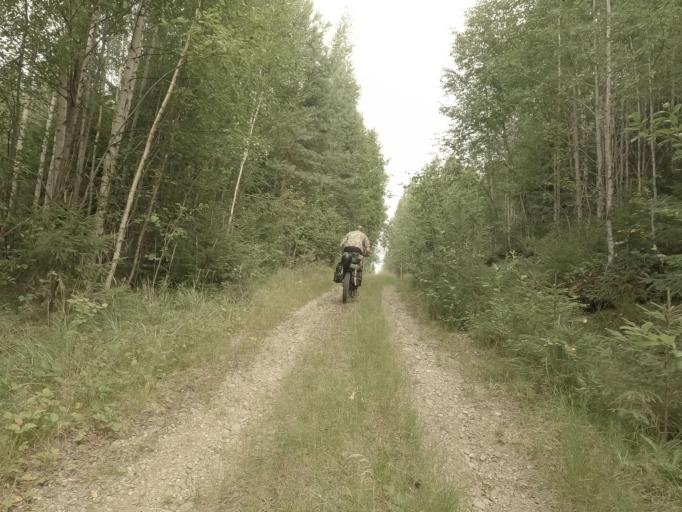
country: RU
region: Leningrad
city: Kamennogorsk
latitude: 61.0200
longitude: 29.1637
